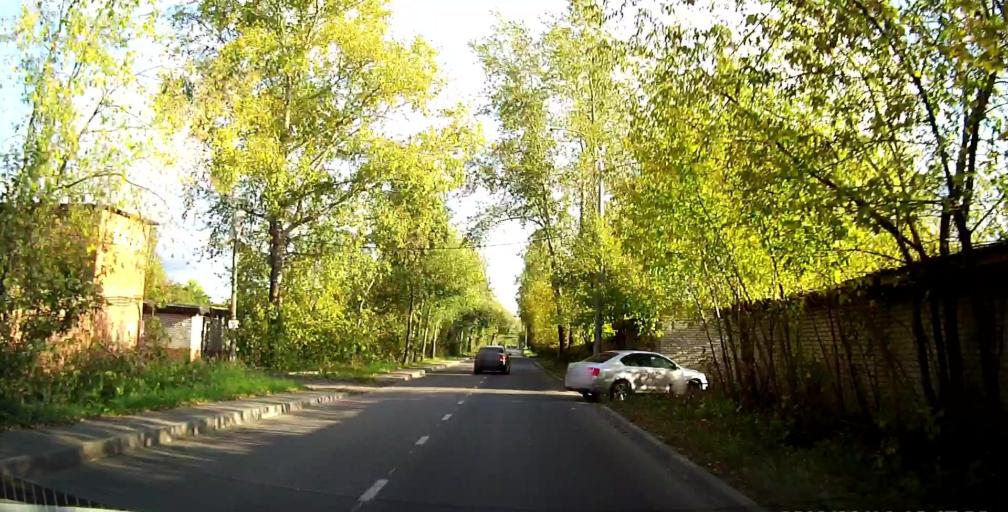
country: RU
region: Moskovskaya
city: Klimovsk
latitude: 55.3639
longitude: 37.5508
